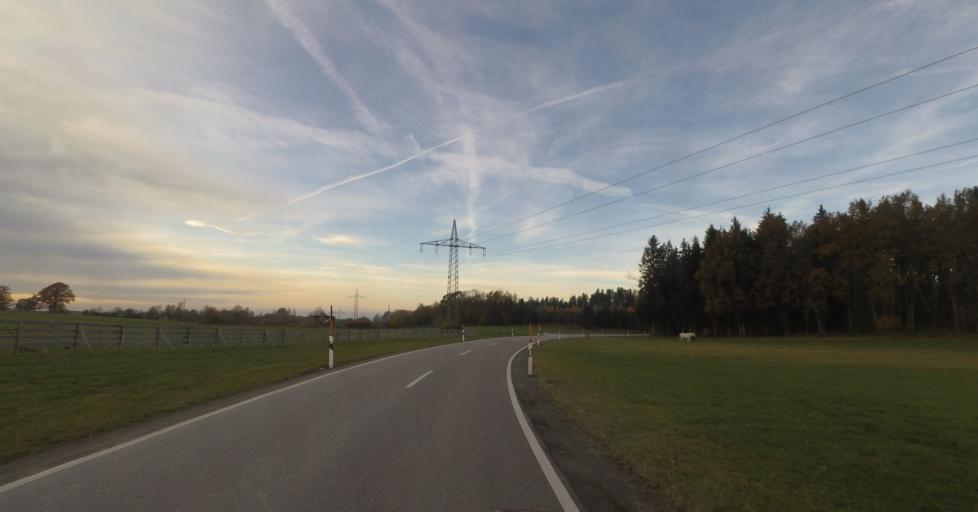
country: DE
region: Bavaria
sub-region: Upper Bavaria
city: Vachendorf
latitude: 47.8718
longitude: 12.6099
